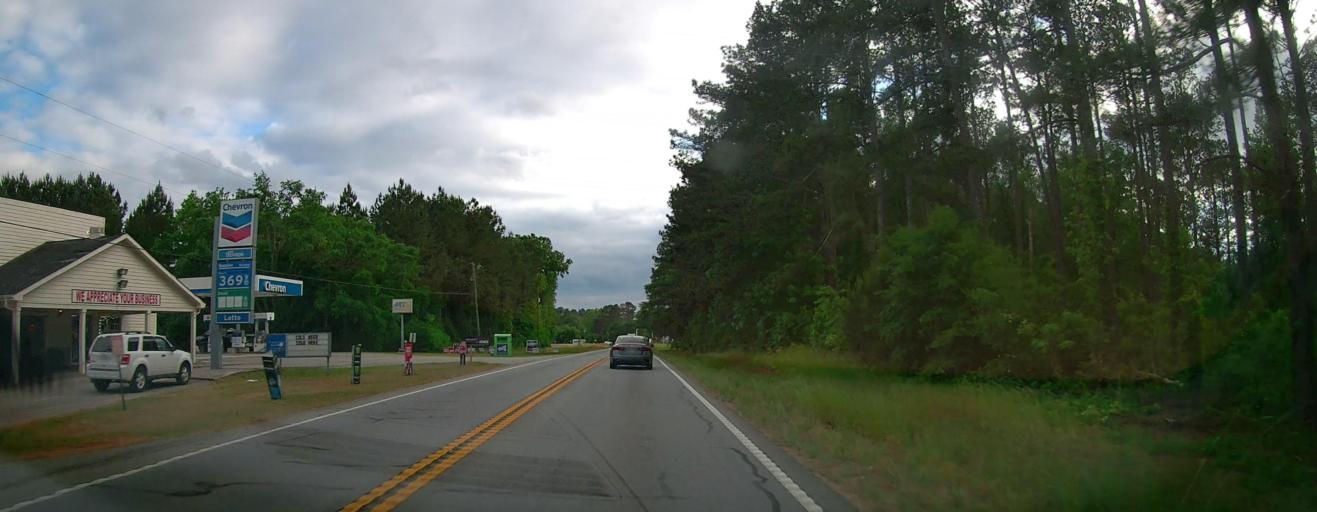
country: US
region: Georgia
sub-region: Oconee County
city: Watkinsville
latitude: 33.8277
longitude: -83.4378
